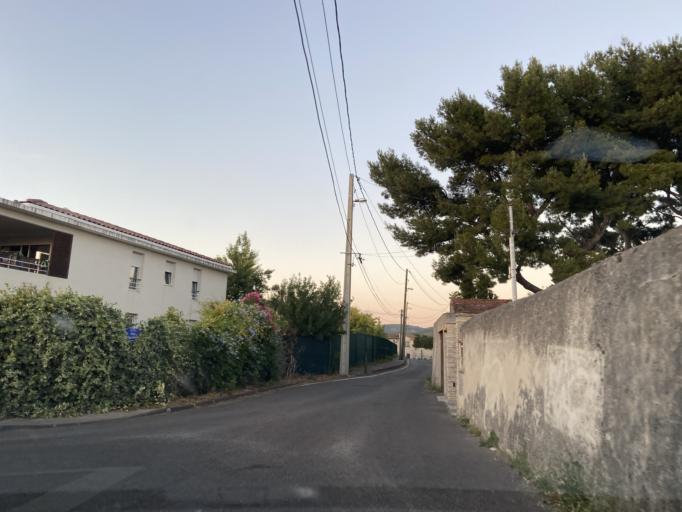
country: FR
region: Provence-Alpes-Cote d'Azur
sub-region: Departement des Bouches-du-Rhone
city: Plan-de-Cuques
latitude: 43.3295
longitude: 5.4498
